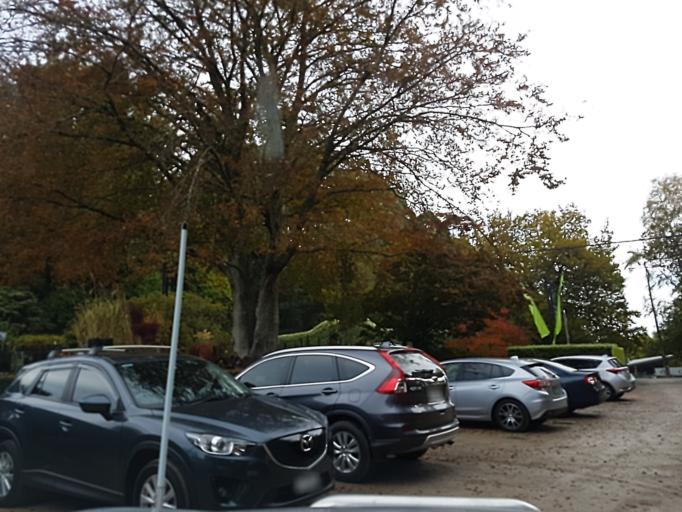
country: AU
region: Victoria
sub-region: Yarra Ranges
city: Olinda
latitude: -37.8606
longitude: 145.3769
